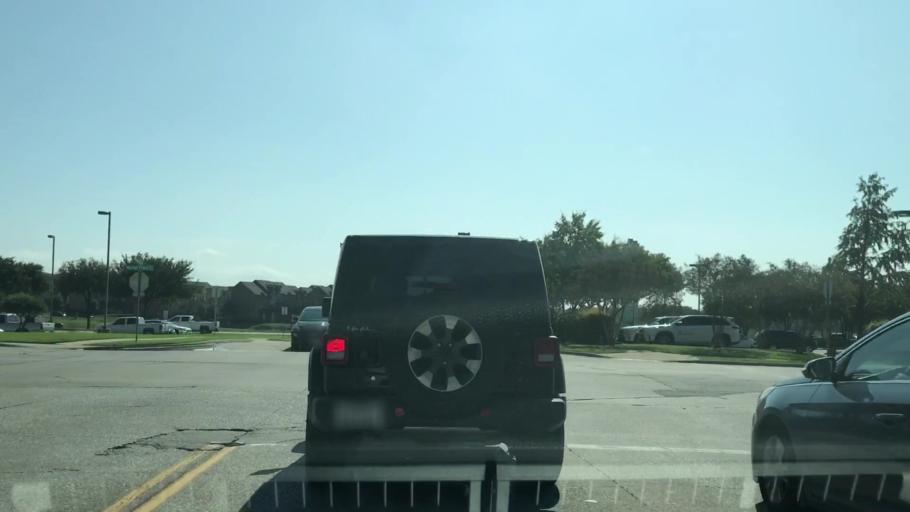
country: US
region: Texas
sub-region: Dallas County
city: Coppell
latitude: 32.9189
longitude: -96.9657
